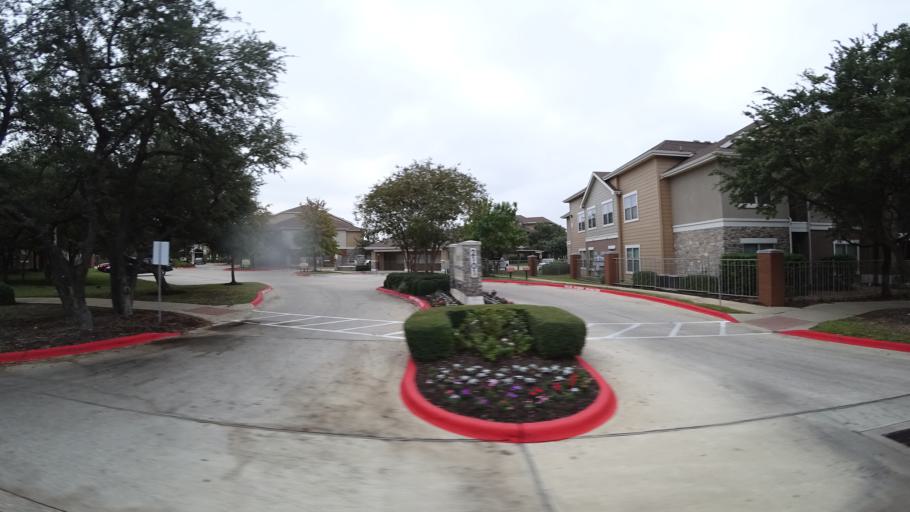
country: US
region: Texas
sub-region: Williamson County
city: Cedar Park
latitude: 30.4801
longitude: -97.8237
